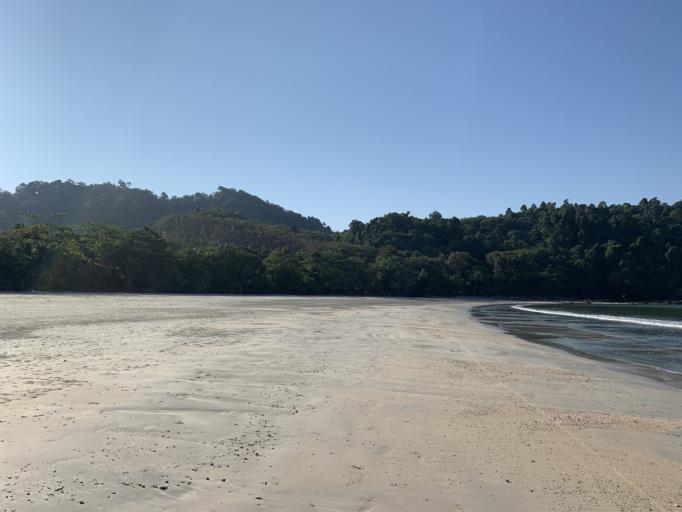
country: TH
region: Ranong
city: Kapoe
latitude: 9.7130
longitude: 98.3969
